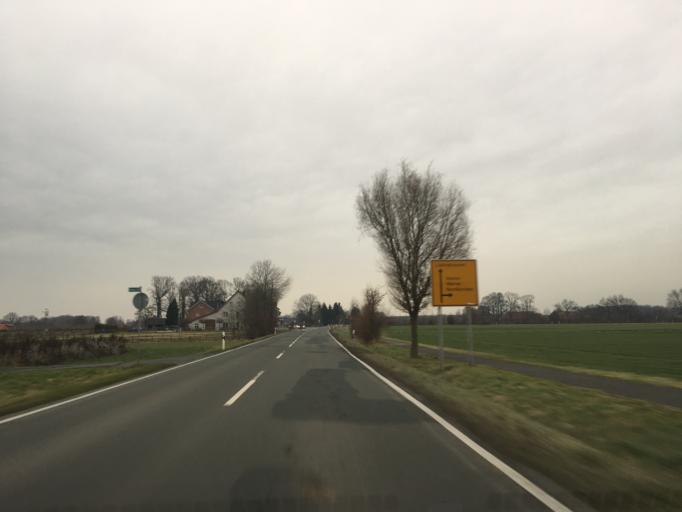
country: DE
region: North Rhine-Westphalia
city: Ludinghausen
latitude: 51.7410
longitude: 7.4754
